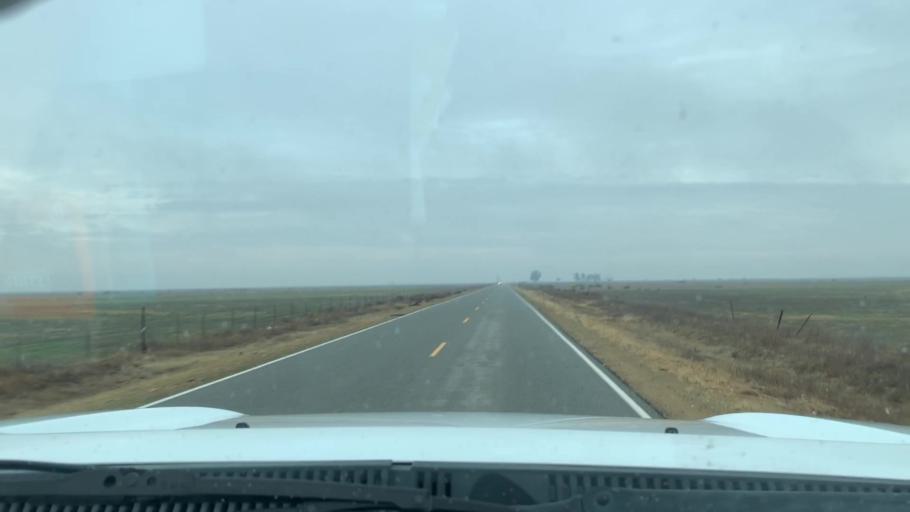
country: US
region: California
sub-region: Kern County
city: Lost Hills
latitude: 35.6556
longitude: -119.5800
